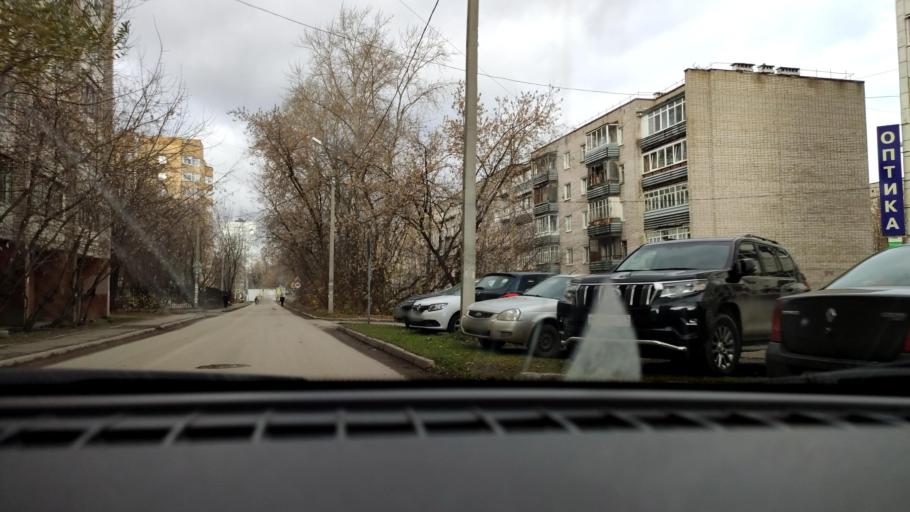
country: RU
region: Perm
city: Perm
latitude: 58.0070
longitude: 56.2689
